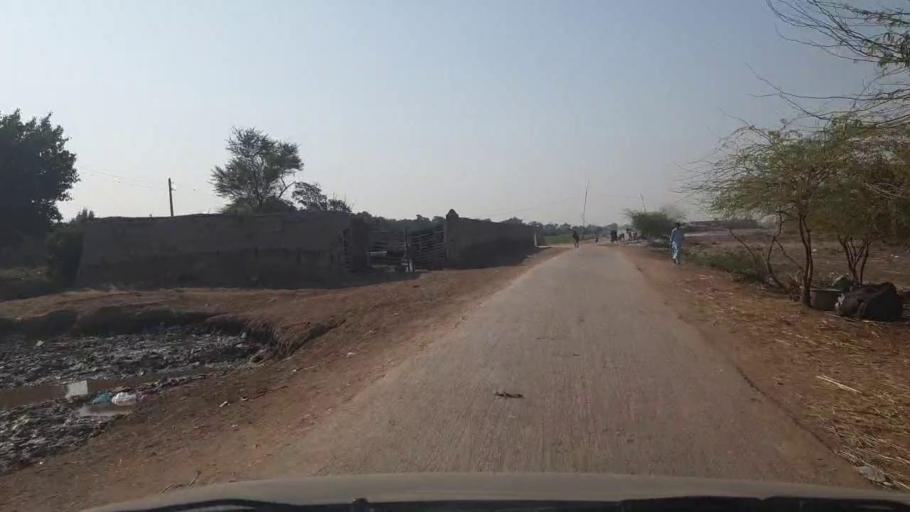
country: PK
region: Sindh
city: Mirwah Gorchani
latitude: 25.3112
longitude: 69.1522
